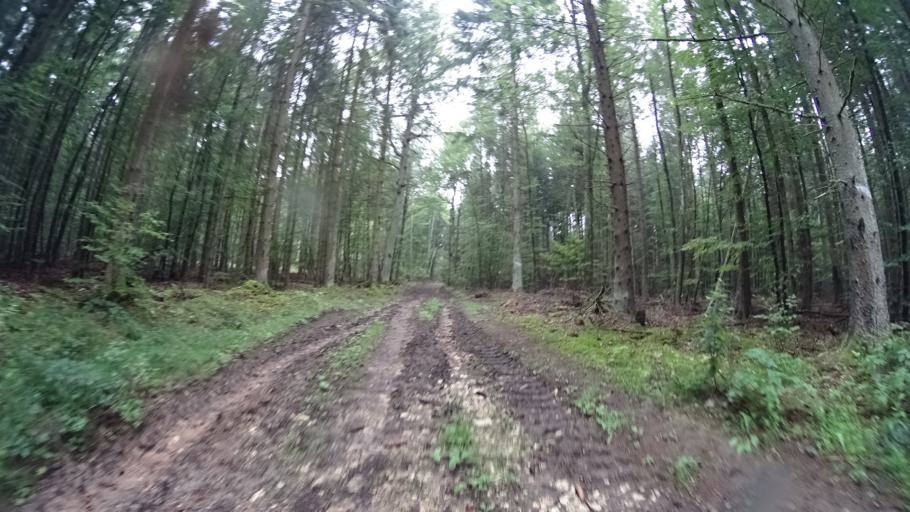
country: DE
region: Bavaria
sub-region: Upper Bavaria
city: Denkendorf
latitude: 48.9200
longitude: 11.3925
